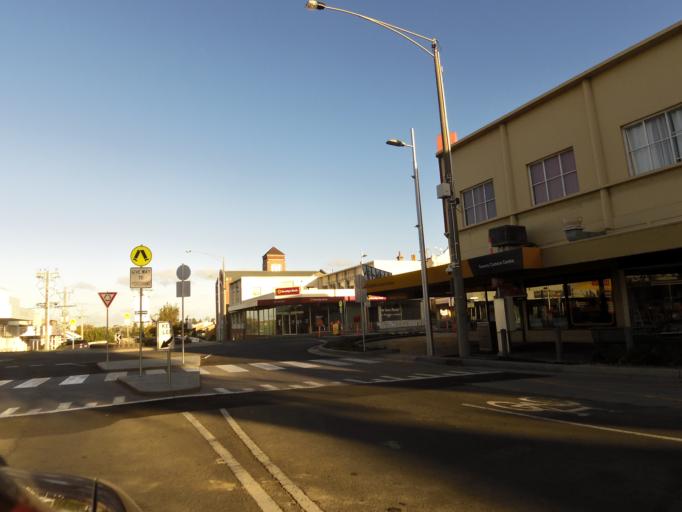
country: AU
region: Victoria
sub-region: Warrnambool
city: Warrnambool
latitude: -38.3835
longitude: 142.4833
